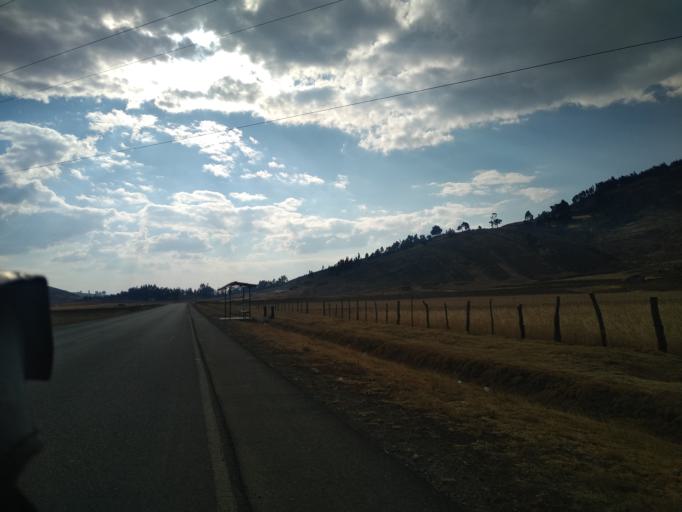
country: PE
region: Cajamarca
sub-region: Provincia de Cajamarca
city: Encanada
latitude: -7.1388
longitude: -78.3837
